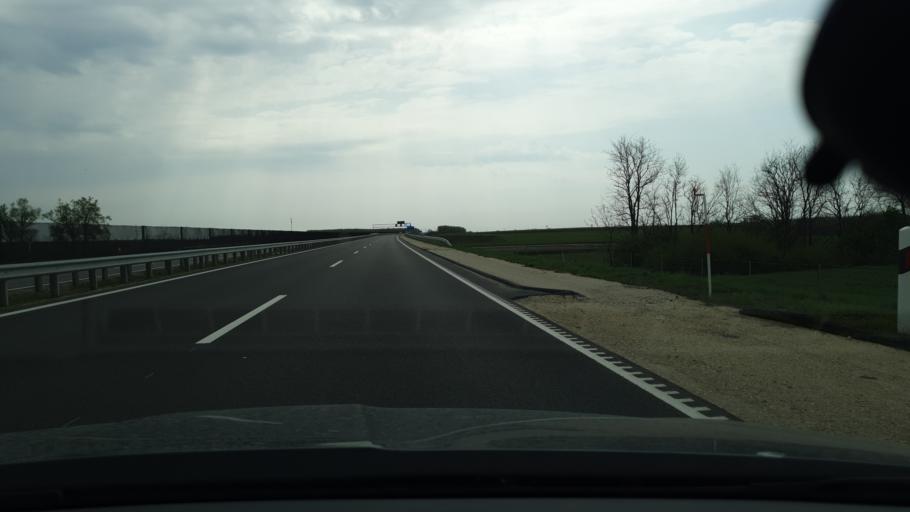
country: HU
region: Pest
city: Pilis
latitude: 47.3229
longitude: 19.5363
